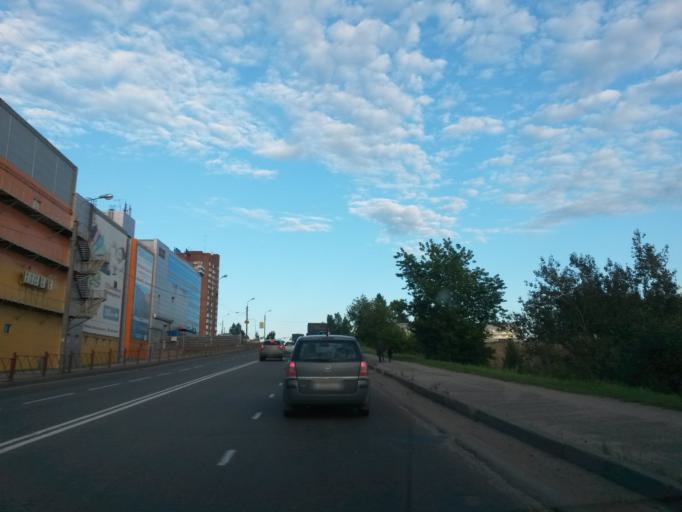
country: RU
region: Jaroslavl
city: Yaroslavl
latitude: 57.5769
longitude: 39.8411
